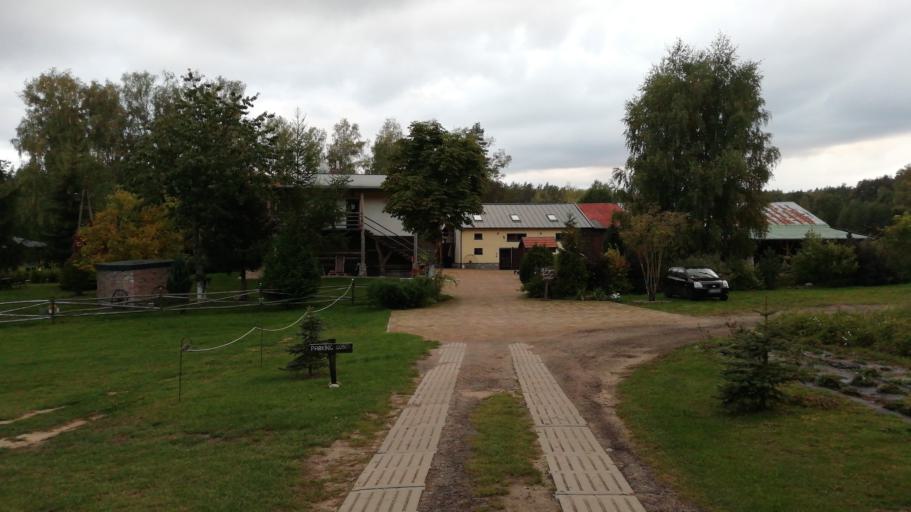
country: PL
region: Pomeranian Voivodeship
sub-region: Powiat czluchowski
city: Rzeczenica
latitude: 53.7336
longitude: 17.1628
